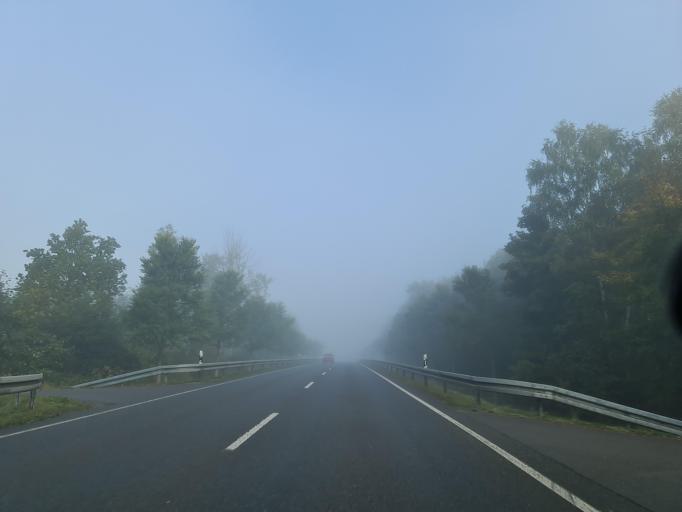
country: DE
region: Thuringia
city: Pormitz
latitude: 50.6295
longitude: 11.8144
